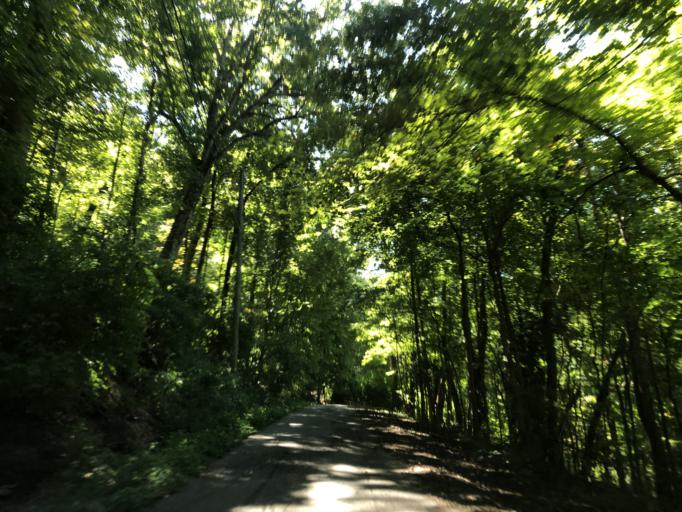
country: US
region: Tennessee
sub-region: Davidson County
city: Oak Hill
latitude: 36.0728
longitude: -86.7876
